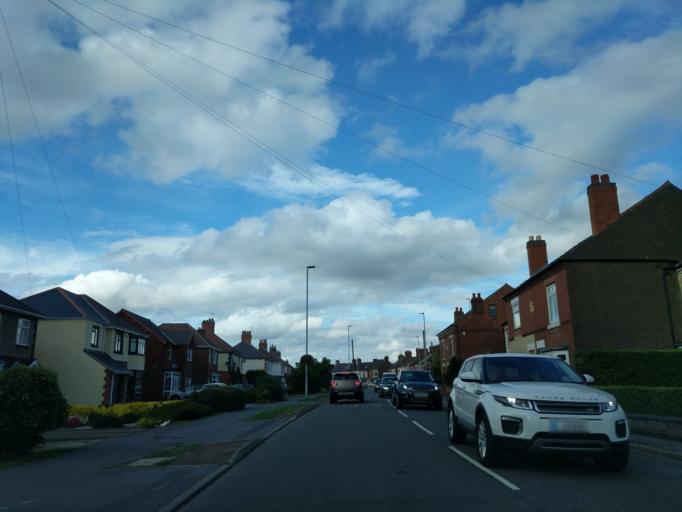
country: GB
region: England
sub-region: Leicestershire
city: Ibstock
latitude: 52.6935
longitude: -1.4023
